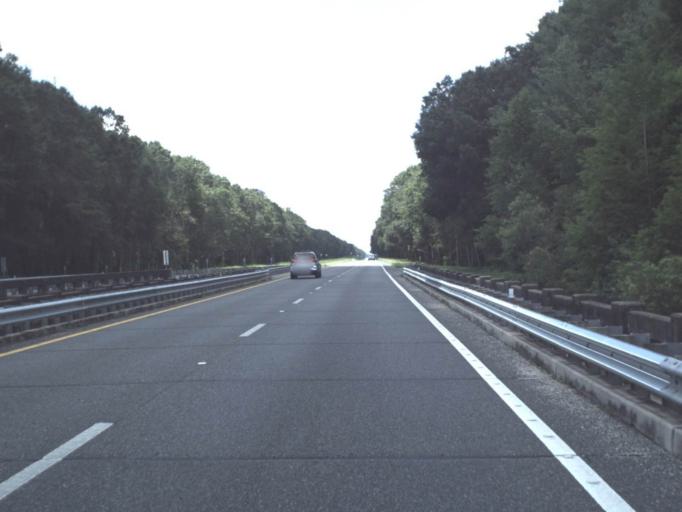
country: US
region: Florida
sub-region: Taylor County
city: Perry
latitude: 30.2509
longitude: -83.7005
